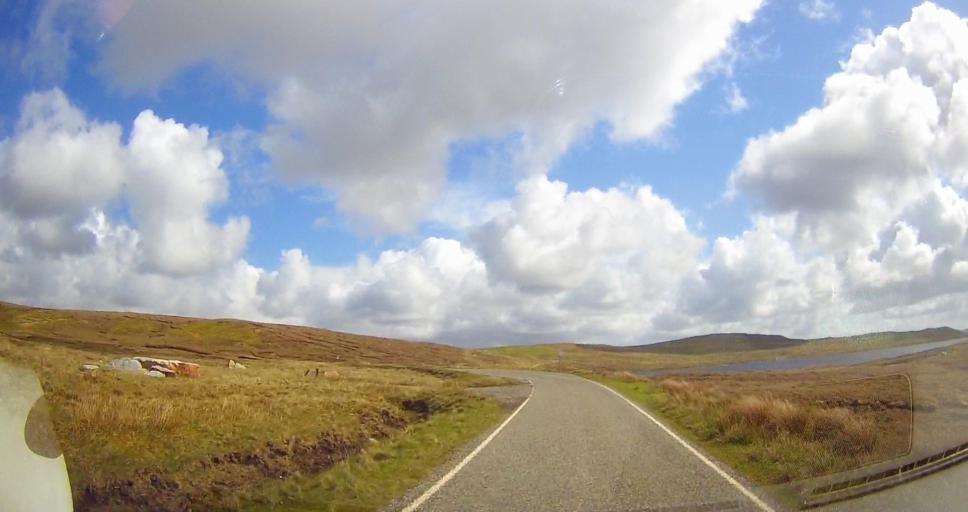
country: GB
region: Scotland
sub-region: Shetland Islands
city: Lerwick
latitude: 60.4971
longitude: -1.3959
